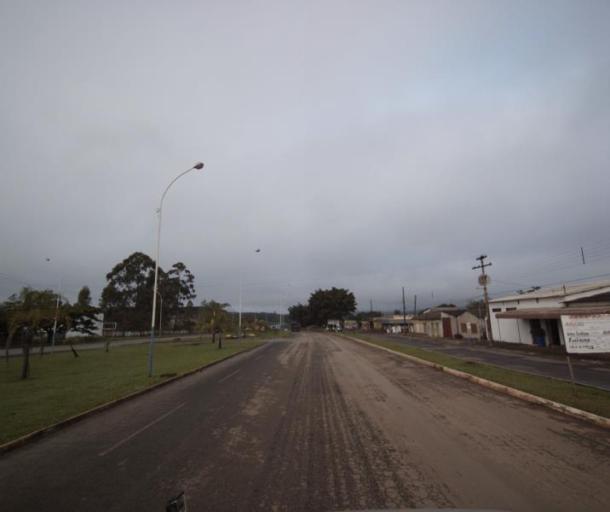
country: BR
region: Goias
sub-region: Pirenopolis
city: Pirenopolis
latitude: -15.7900
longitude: -48.7725
